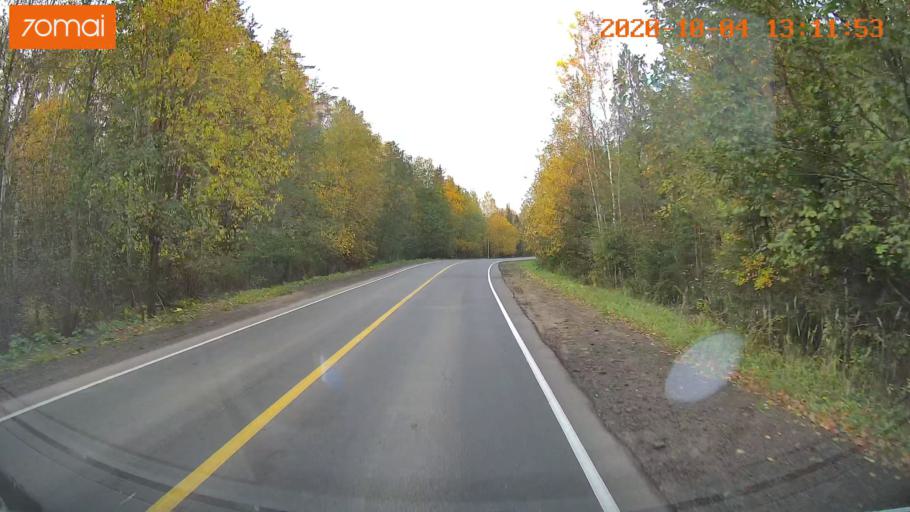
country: RU
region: Ivanovo
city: Bogorodskoye
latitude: 57.0798
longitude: 40.9359
